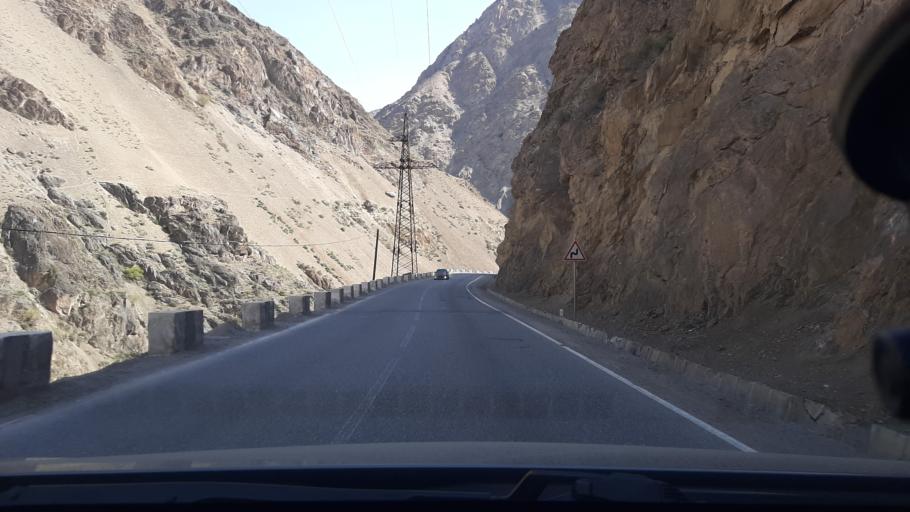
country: TJ
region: Viloyati Sughd
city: Ayni
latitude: 39.3304
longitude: 68.5485
